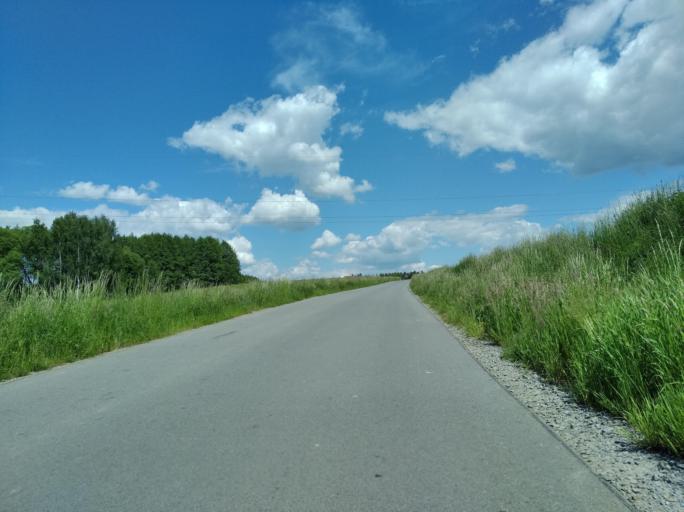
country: PL
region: Subcarpathian Voivodeship
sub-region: Powiat jasielski
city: Tarnowiec
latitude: 49.7707
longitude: 21.6115
